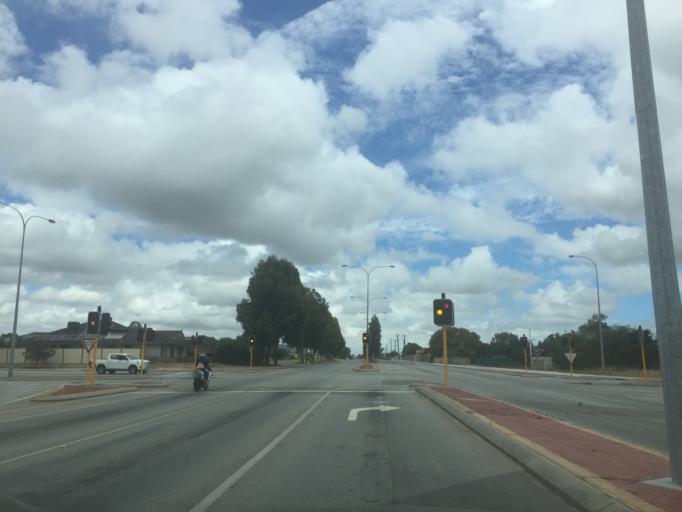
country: AU
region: Western Australia
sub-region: Gosnells
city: Thornlie
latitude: -32.0825
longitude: 115.9520
